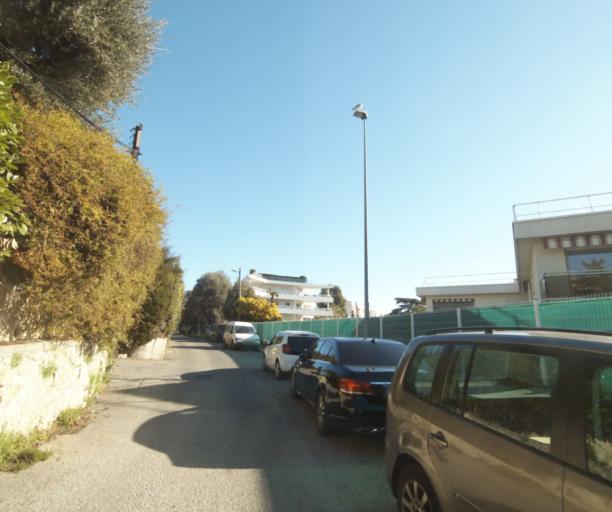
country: FR
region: Provence-Alpes-Cote d'Azur
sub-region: Departement des Alpes-Maritimes
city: Antibes
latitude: 43.5732
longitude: 7.1062
